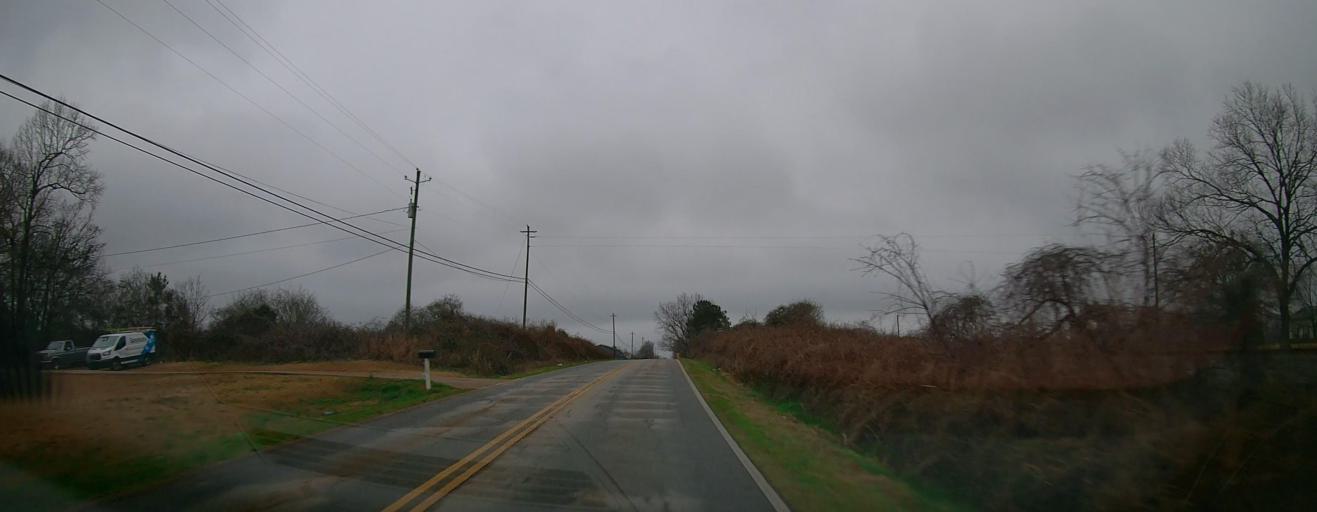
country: US
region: Georgia
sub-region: Lamar County
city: Barnesville
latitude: 33.1430
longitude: -84.1954
